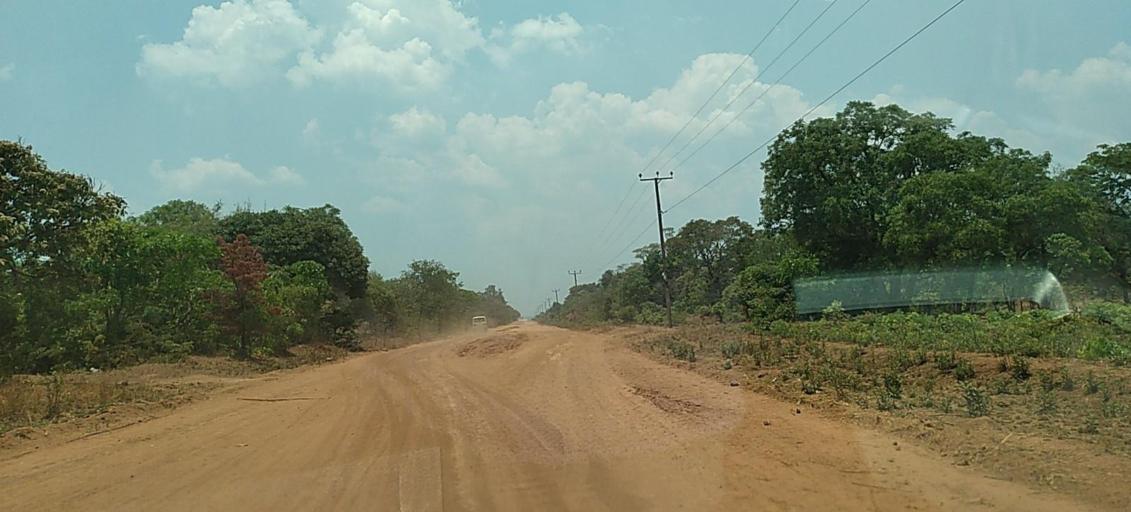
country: ZM
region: Copperbelt
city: Chingola
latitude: -12.9028
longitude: 27.5709
